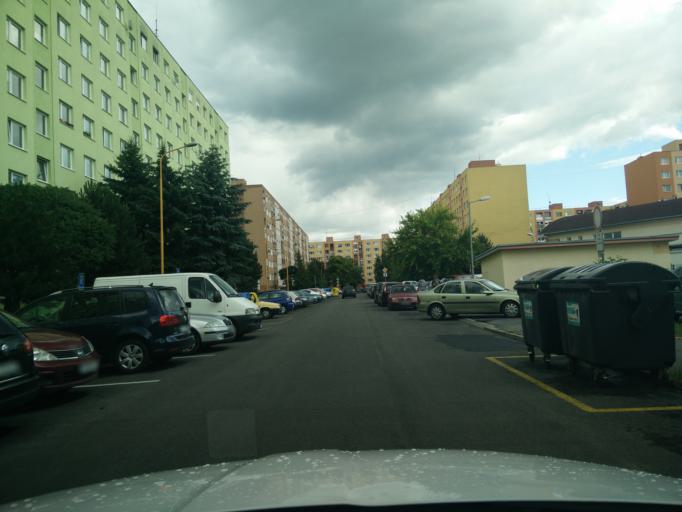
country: SK
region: Nitriansky
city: Prievidza
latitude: 48.7848
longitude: 18.6209
